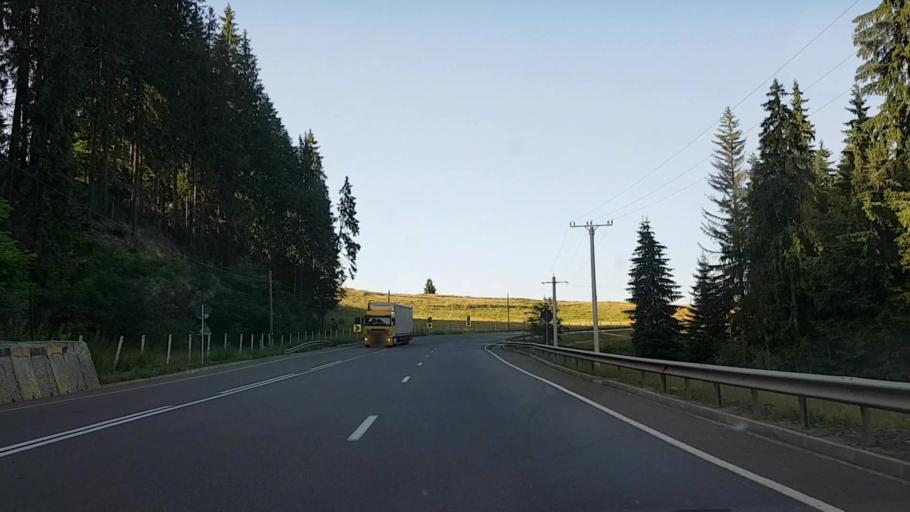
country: RO
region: Bistrita-Nasaud
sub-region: Comuna Lunca Ilvei
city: Lunca Ilvei
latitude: 47.2291
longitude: 24.9767
